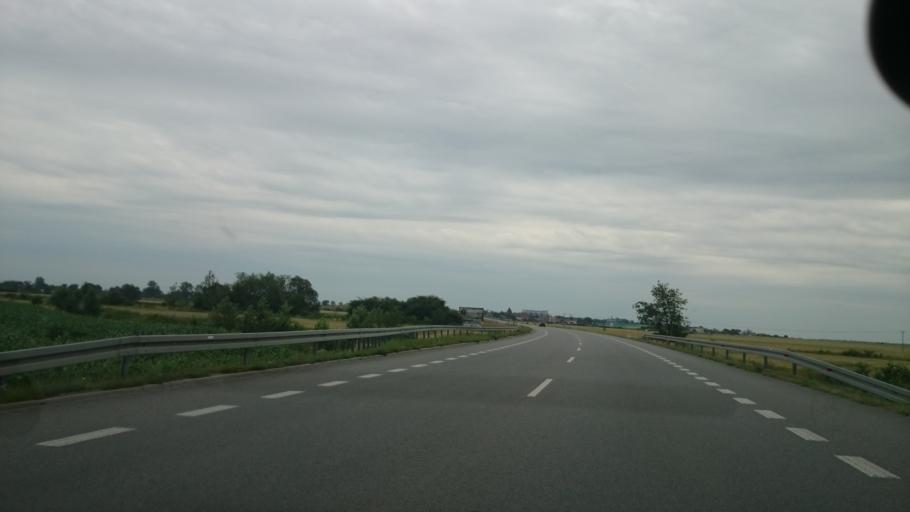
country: PL
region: Opole Voivodeship
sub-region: Powiat brzeski
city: Grodkow
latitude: 50.6867
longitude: 17.3680
